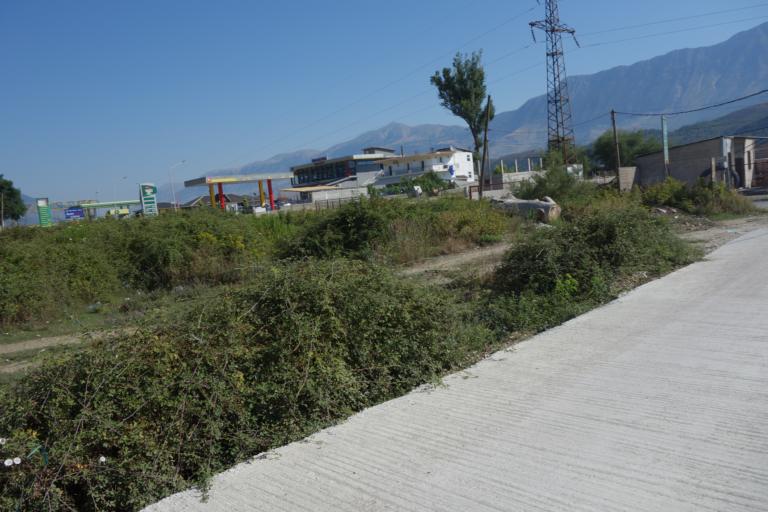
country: AL
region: Gjirokaster
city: Gjirokaster
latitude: 40.0881
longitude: 20.1398
